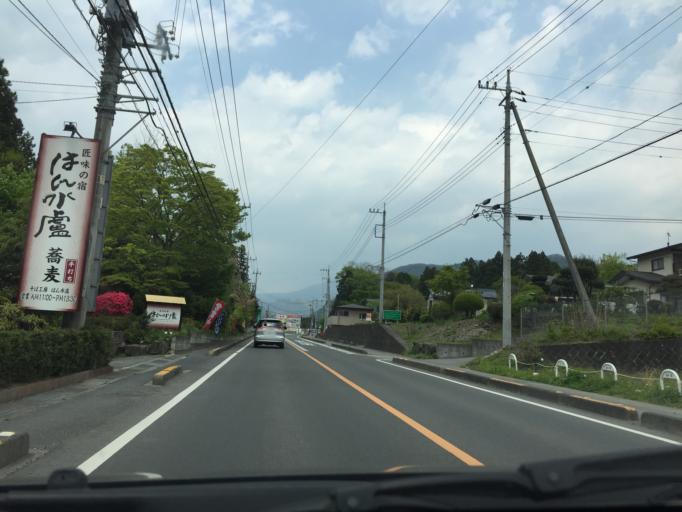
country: JP
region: Tochigi
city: Imaichi
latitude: 36.8108
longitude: 139.7103
